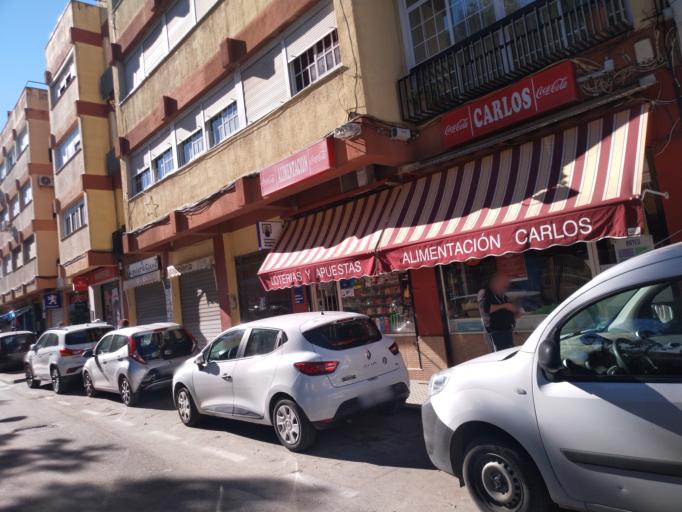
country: ES
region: Andalusia
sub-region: Provincia de Cadiz
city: San Fernando
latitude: 36.4769
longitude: -6.1948
